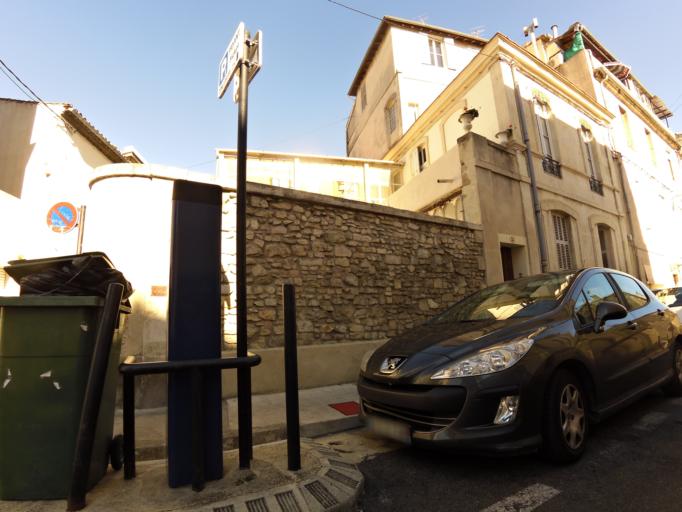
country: FR
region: Languedoc-Roussillon
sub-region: Departement du Gard
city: Nimes
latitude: 43.8371
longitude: 4.3643
